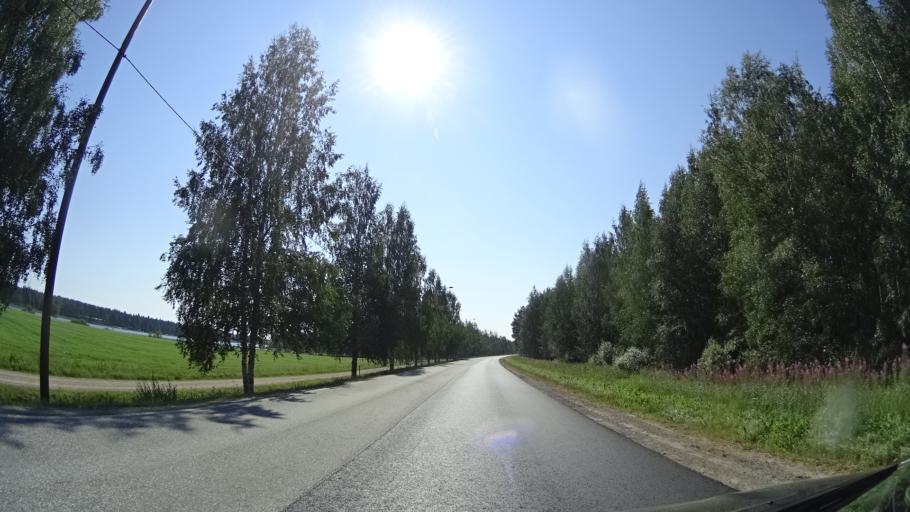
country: FI
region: North Karelia
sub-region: Joensuu
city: Juuka
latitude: 63.2447
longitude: 29.2727
